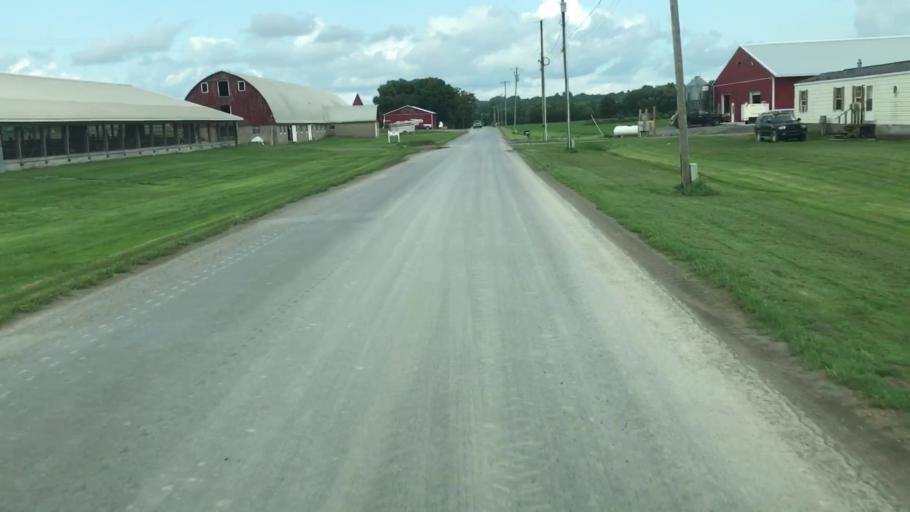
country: US
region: New York
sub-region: Onondaga County
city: Elbridge
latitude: 42.9860
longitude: -76.4693
